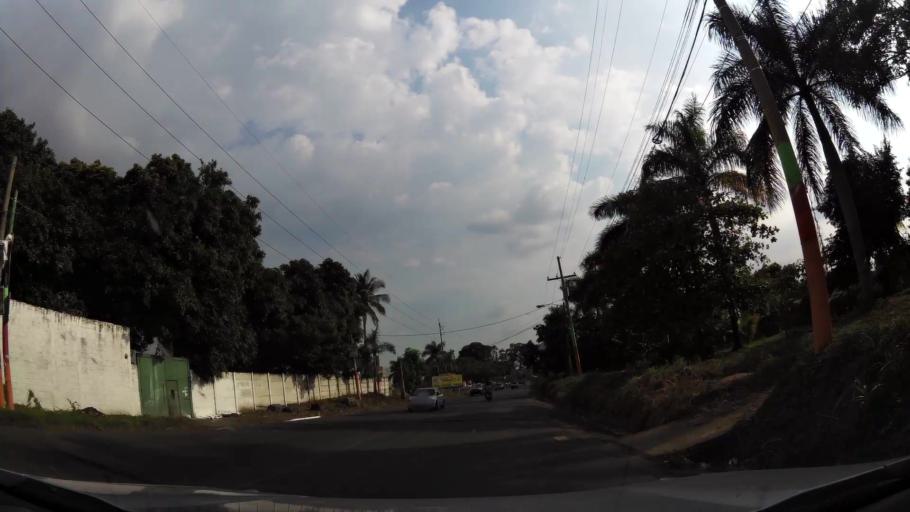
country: GT
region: Escuintla
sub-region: Municipio de Escuintla
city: Escuintla
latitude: 14.3200
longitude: -90.7937
